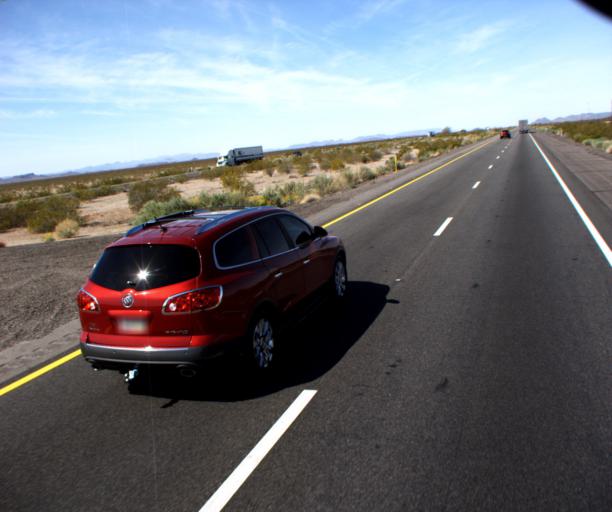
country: US
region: Arizona
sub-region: La Paz County
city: Salome
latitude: 33.5828
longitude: -113.4422
